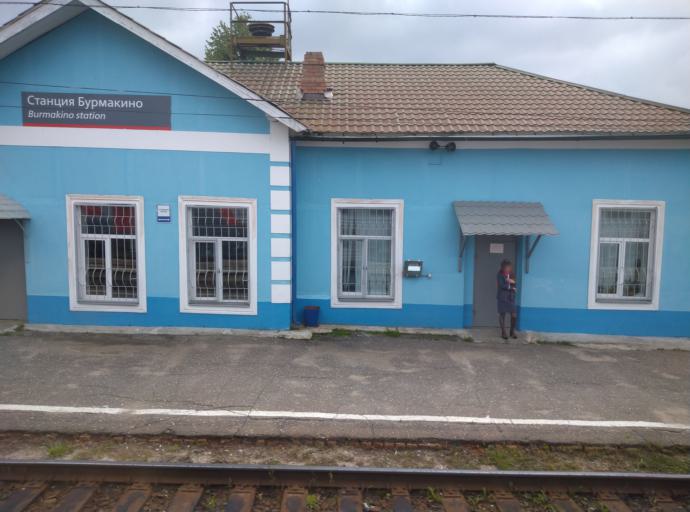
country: RU
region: Jaroslavl
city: Burmakino
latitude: 57.4368
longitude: 40.3192
